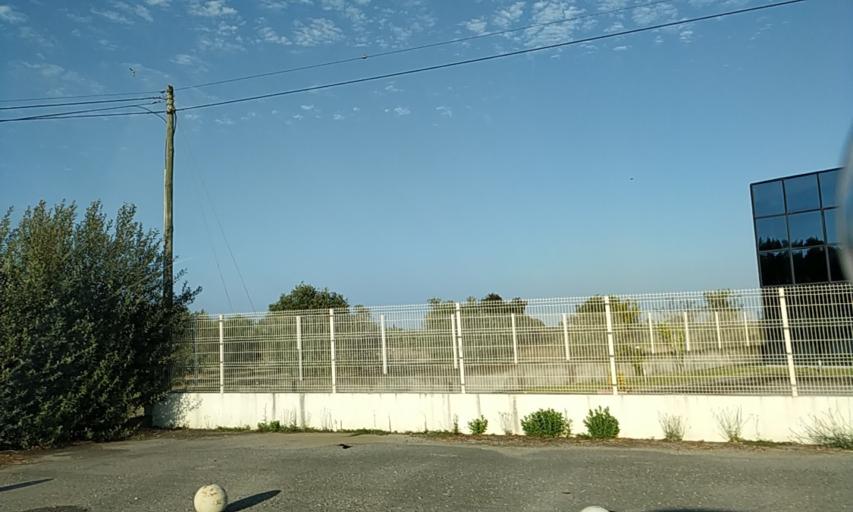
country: PT
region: Santarem
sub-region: Alcanena
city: Alcanena
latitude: 39.4384
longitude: -8.6256
